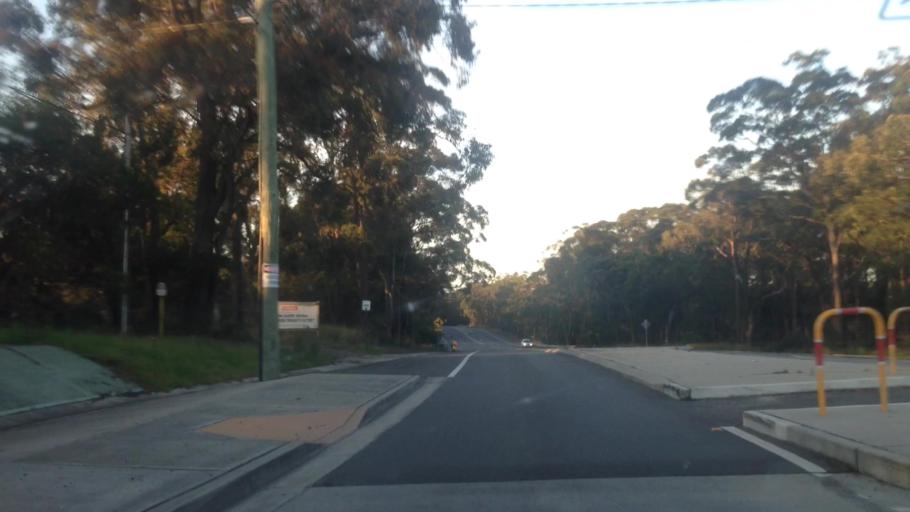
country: AU
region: New South Wales
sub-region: Wyong Shire
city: Charmhaven
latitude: -33.1560
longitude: 151.4787
